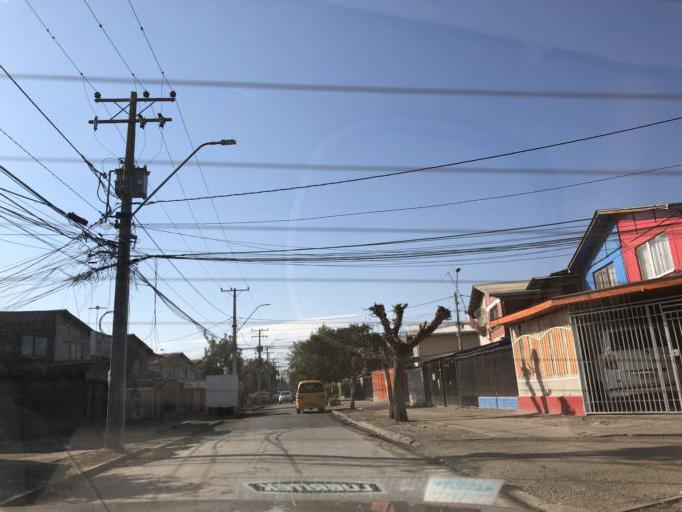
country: CL
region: Santiago Metropolitan
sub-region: Provincia de Santiago
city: La Pintana
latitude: -33.6307
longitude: -70.6238
